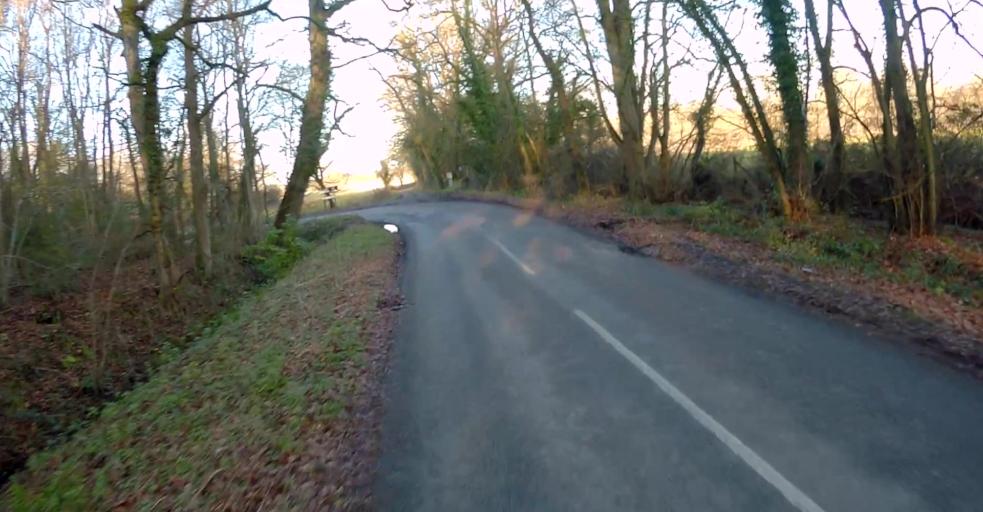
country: GB
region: England
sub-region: Hampshire
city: Hook
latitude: 51.2940
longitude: -0.9767
